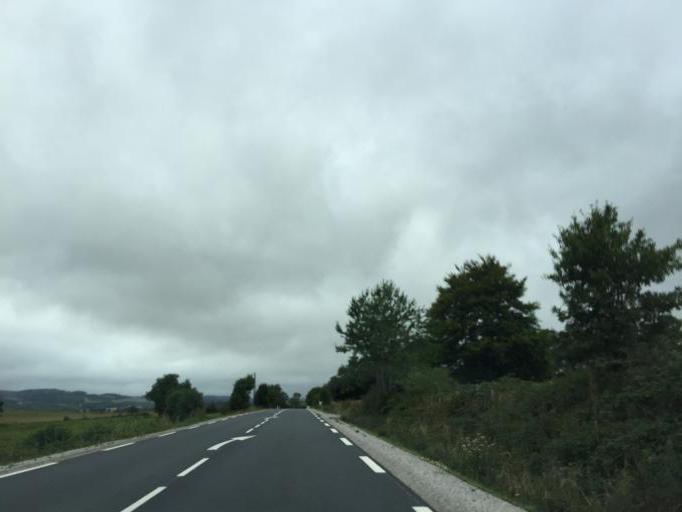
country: FR
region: Midi-Pyrenees
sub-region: Departement de l'Aveyron
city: Severac-le-Chateau
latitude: 44.2402
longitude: 2.9547
